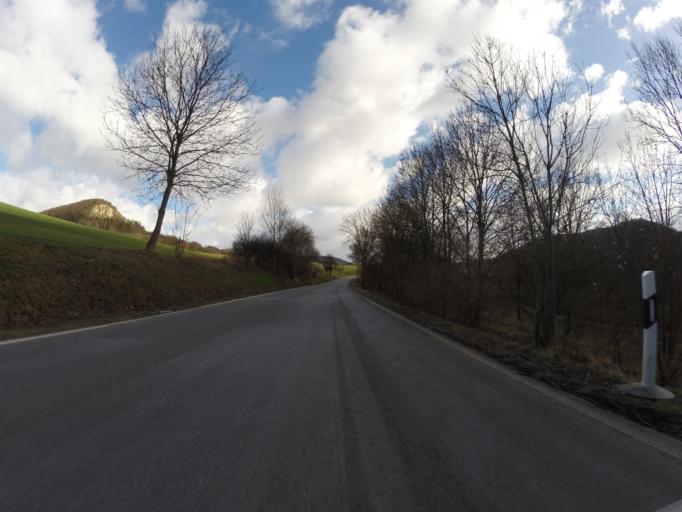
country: DE
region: Thuringia
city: Loberschutz
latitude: 50.9686
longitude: 11.6942
